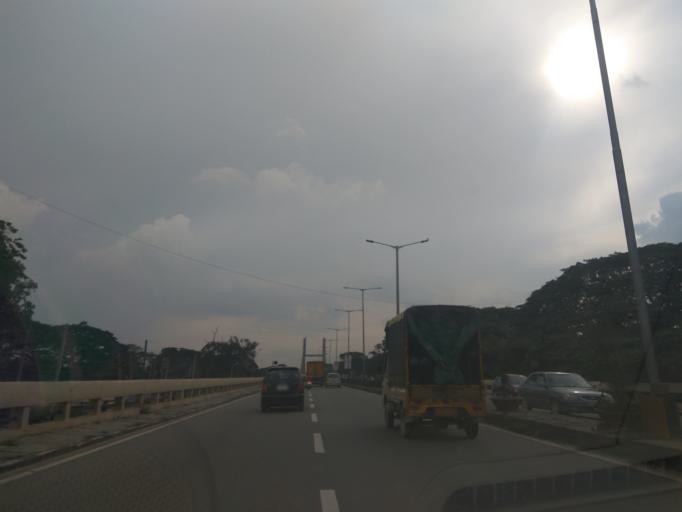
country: IN
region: Karnataka
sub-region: Bangalore Urban
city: Bangalore
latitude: 13.0038
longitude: 77.6830
